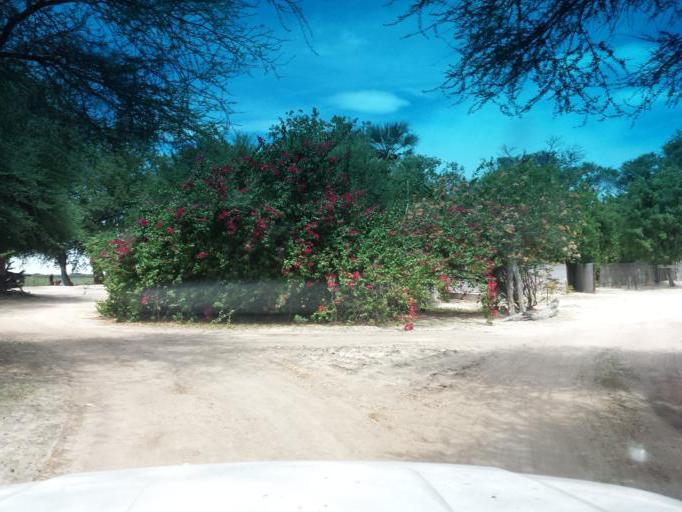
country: BW
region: North West
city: Shakawe
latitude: -18.7458
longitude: 22.1964
